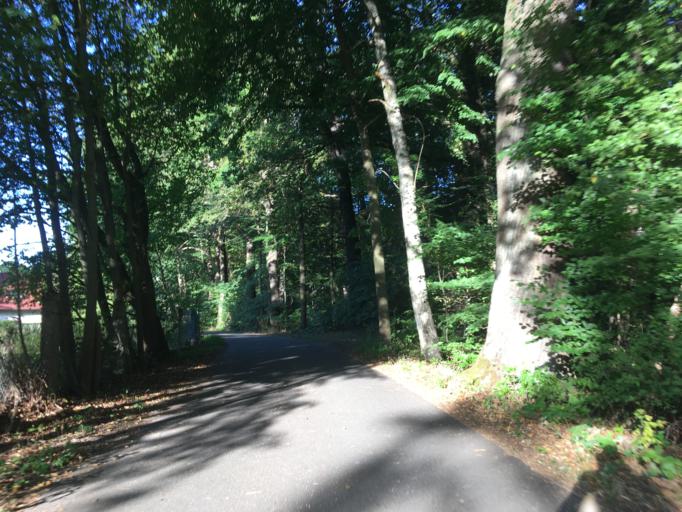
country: DE
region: Saxony
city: Bad Muskau
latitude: 51.5608
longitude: 14.7089
